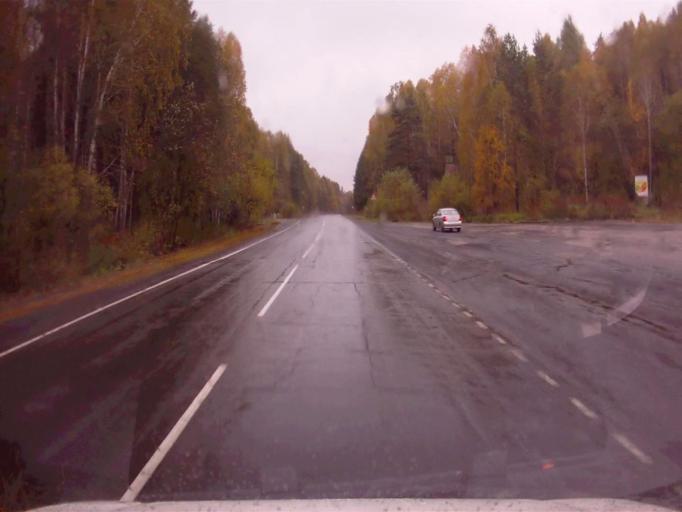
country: RU
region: Chelyabinsk
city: Verkhniy Ufaley
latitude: 55.9513
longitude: 60.4000
